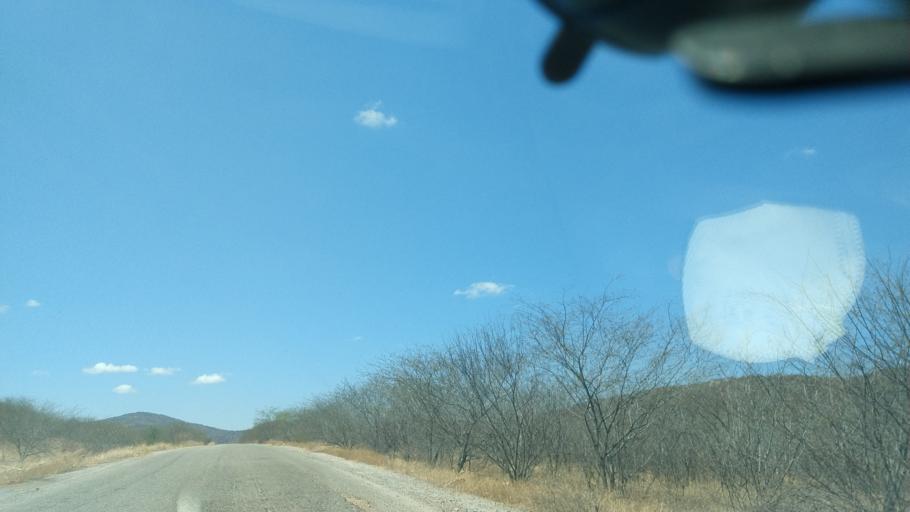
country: BR
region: Rio Grande do Norte
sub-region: Sao Tome
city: Sao Tome
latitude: -5.9712
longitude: -36.1340
